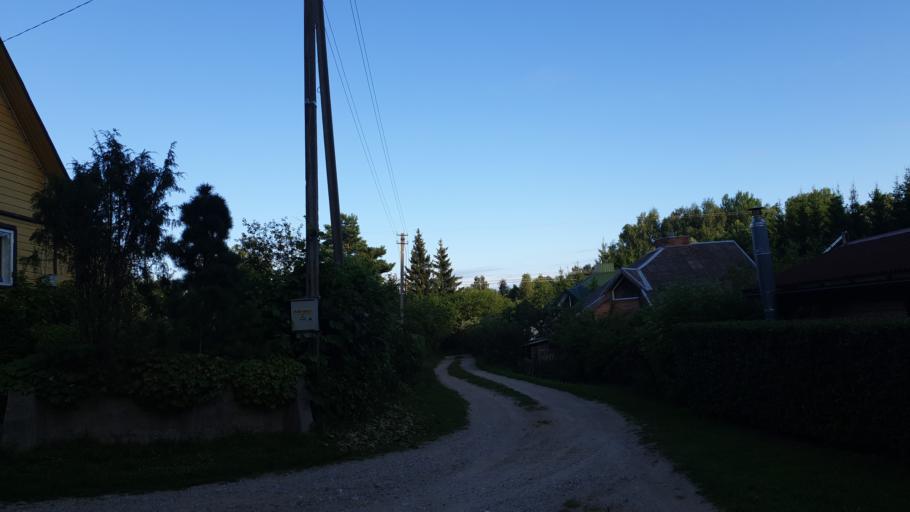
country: LT
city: Grigiskes
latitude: 54.7635
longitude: 25.0185
